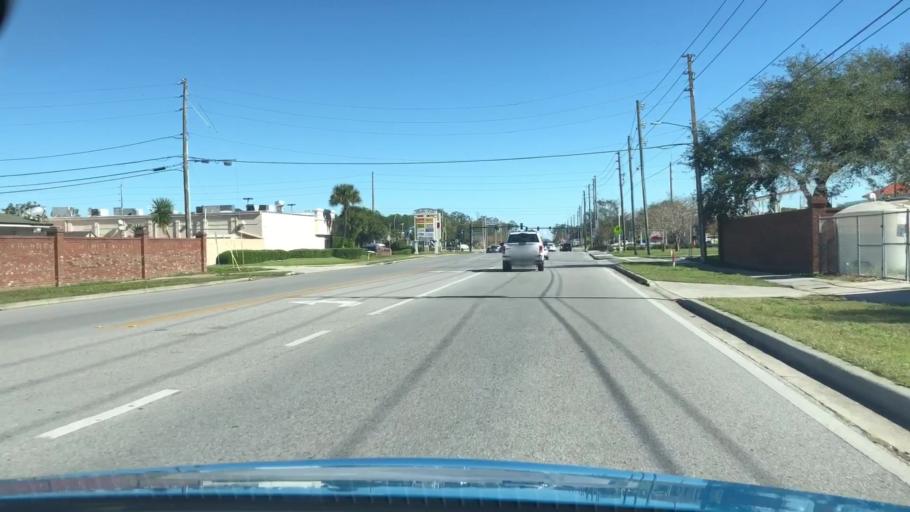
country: US
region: Florida
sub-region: Orange County
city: Conway
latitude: 28.4805
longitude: -81.3333
